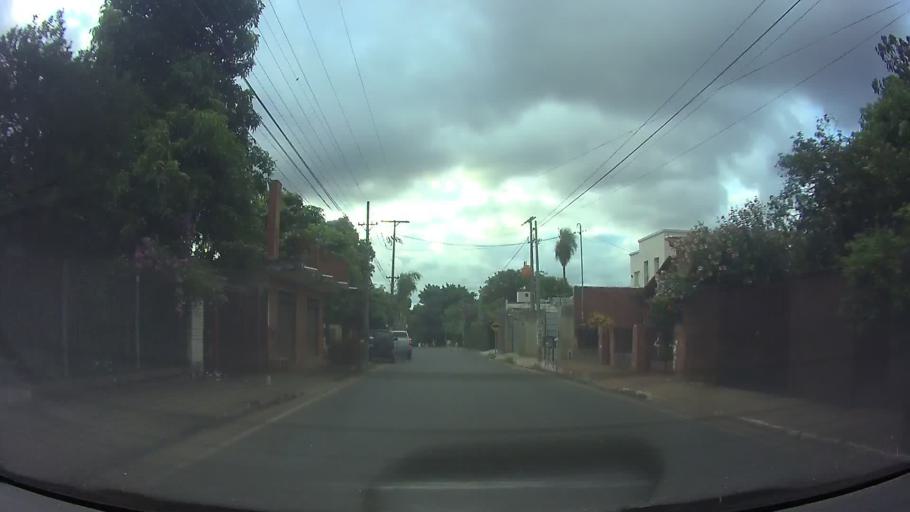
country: PY
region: Central
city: Fernando de la Mora
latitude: -25.3145
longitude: -57.5494
